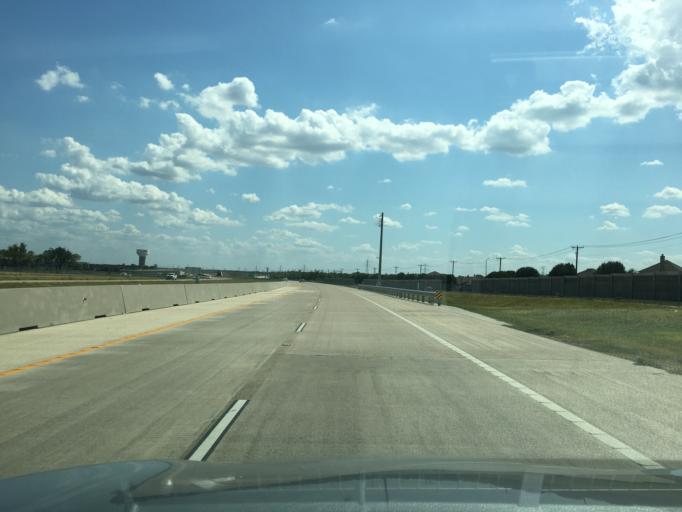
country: US
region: Texas
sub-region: Tarrant County
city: Mansfield
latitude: 32.6188
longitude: -97.0756
